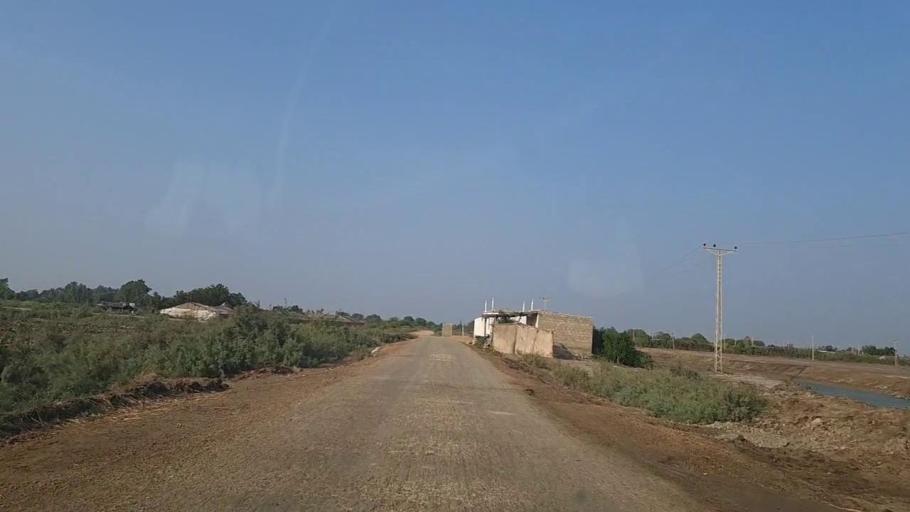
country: PK
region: Sindh
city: Mirpur Sakro
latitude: 24.5687
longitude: 67.6701
